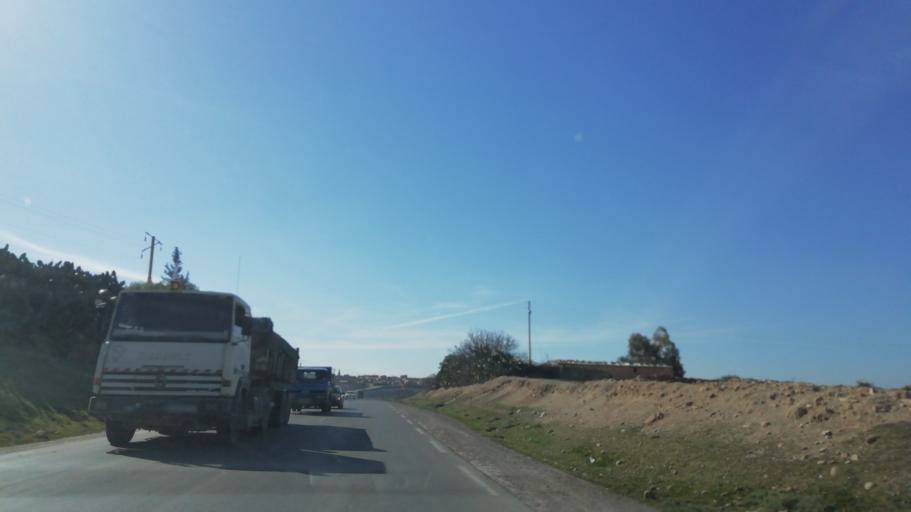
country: DZ
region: Mascara
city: Oued el Abtal
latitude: 35.4555
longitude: 0.7263
